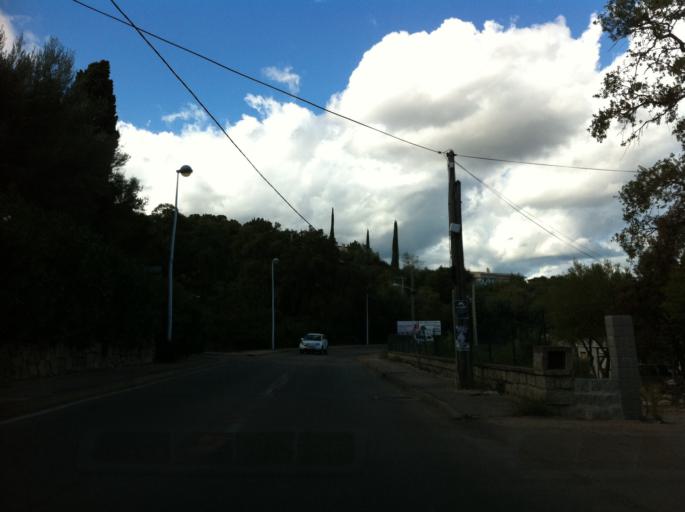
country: FR
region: Corsica
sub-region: Departement de la Corse-du-Sud
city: Porto-Vecchio
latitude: 41.6213
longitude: 9.2840
